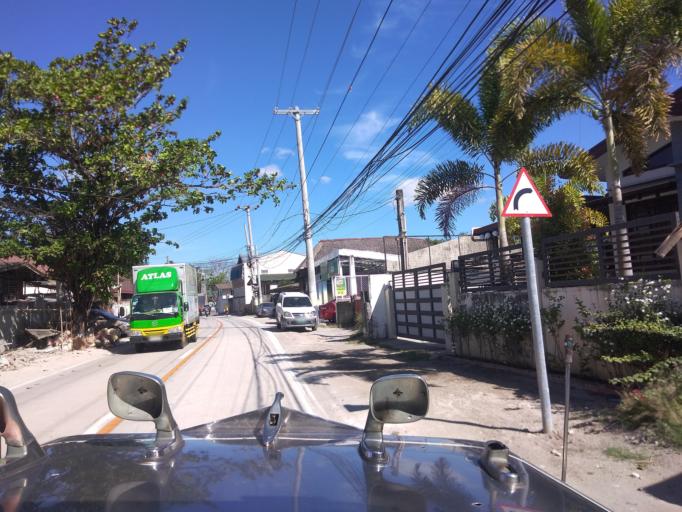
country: PH
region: Central Luzon
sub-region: Province of Pampanga
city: Santa Rita
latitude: 14.9956
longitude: 120.6167
